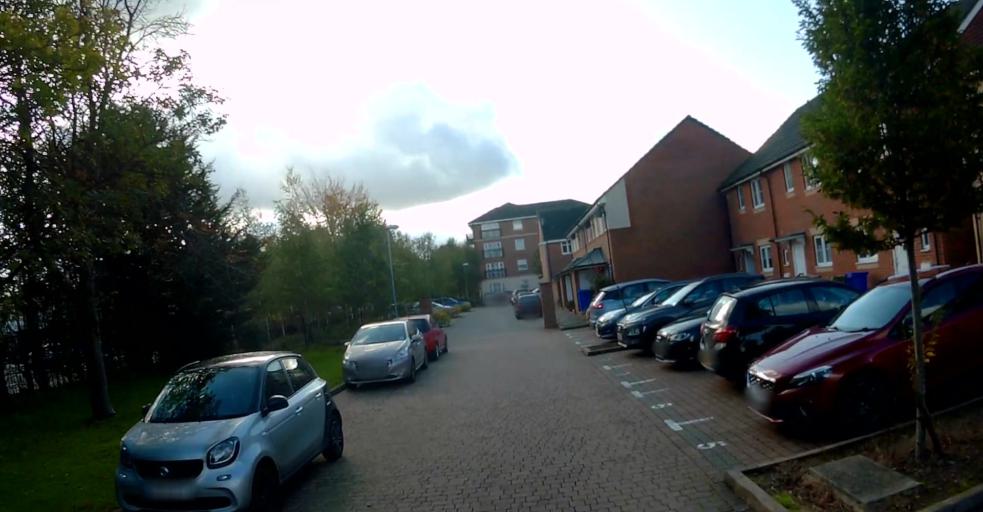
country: GB
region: England
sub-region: Hampshire
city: Farnborough
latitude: 51.2751
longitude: -0.7564
